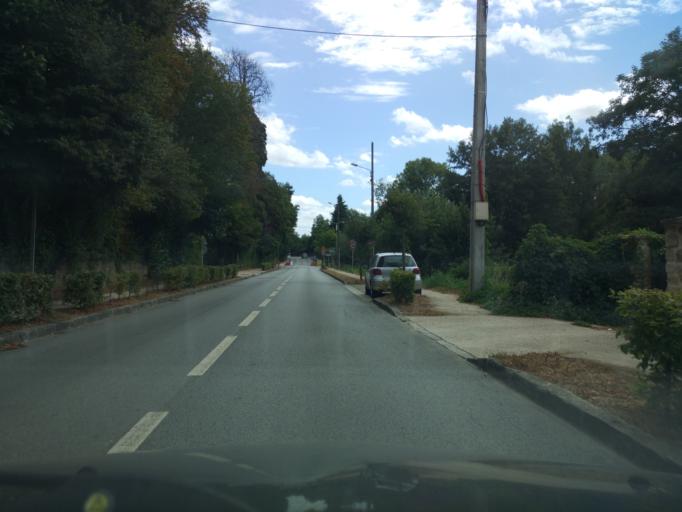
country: FR
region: Ile-de-France
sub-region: Departement des Yvelines
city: Saint-Remy-les-Chevreuse
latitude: 48.7063
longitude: 2.0877
